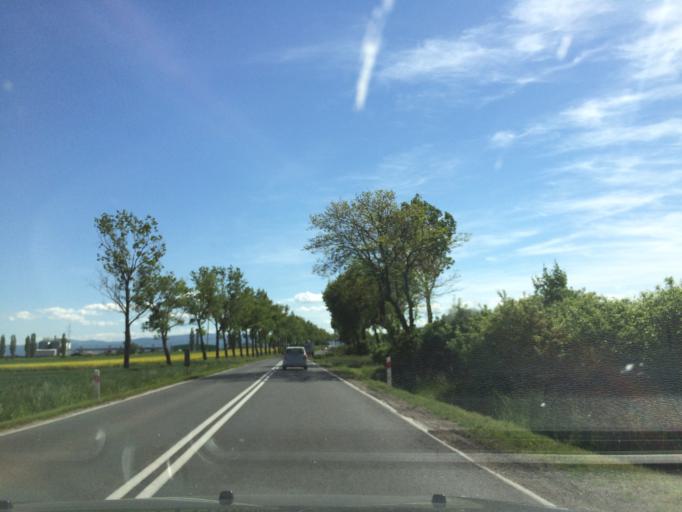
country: PL
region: Lower Silesian Voivodeship
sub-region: Powiat swidnicki
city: Swidnica
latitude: 50.8654
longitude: 16.5588
